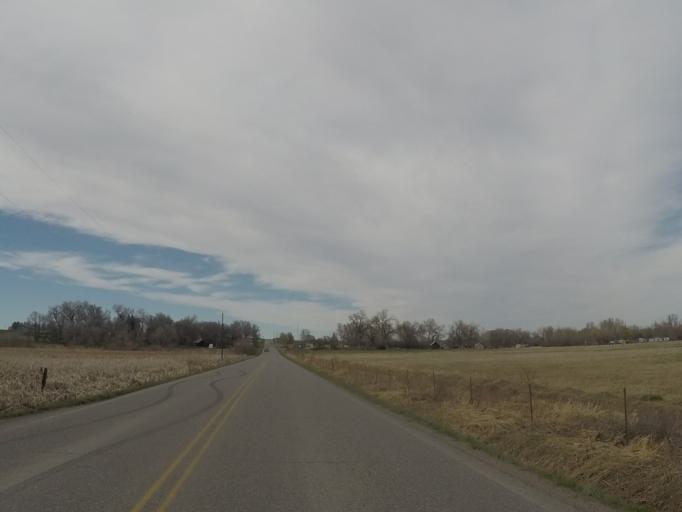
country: US
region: Montana
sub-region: Yellowstone County
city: Laurel
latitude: 45.7073
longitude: -108.6587
